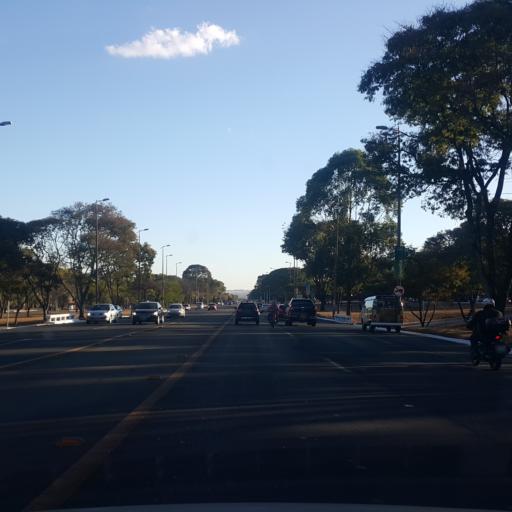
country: BR
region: Federal District
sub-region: Brasilia
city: Brasilia
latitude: -15.8246
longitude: -47.9114
